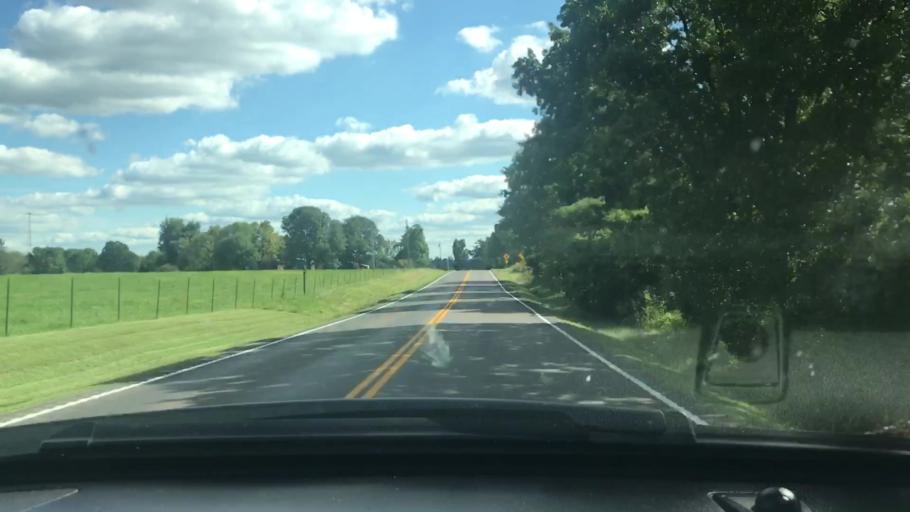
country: US
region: Missouri
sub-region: Wright County
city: Mountain Grove
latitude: 37.2592
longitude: -92.3082
